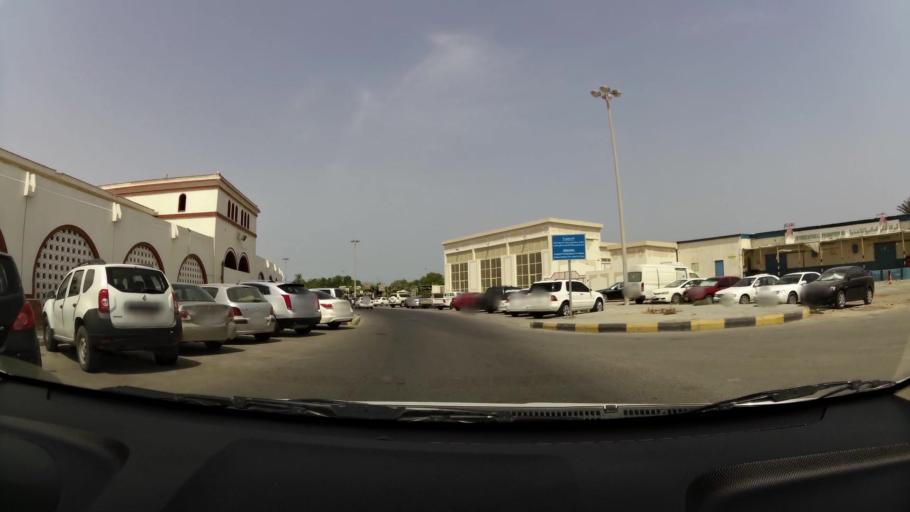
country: AE
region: Ash Shariqah
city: Sharjah
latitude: 25.3519
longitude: 55.3823
